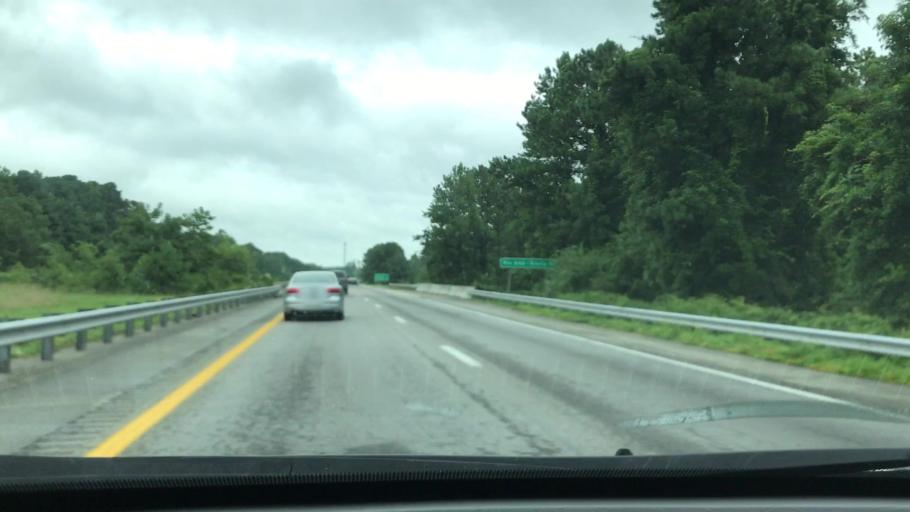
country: US
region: Virginia
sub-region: City of Emporia
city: Emporia
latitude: 36.8158
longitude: -77.4561
